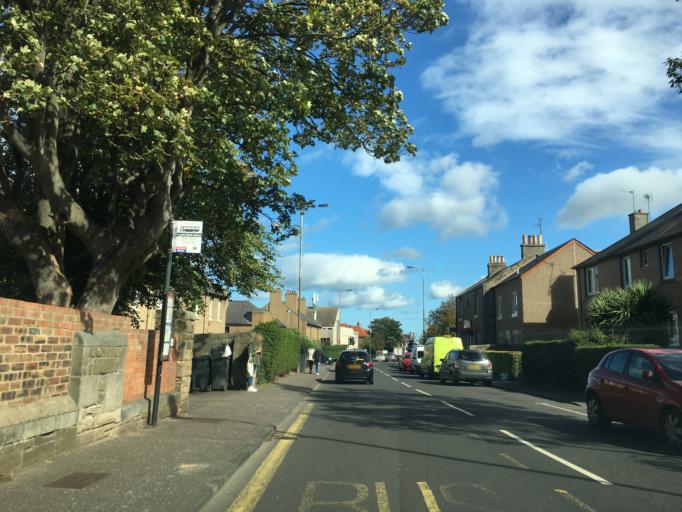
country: GB
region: Scotland
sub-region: Midlothian
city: Loanhead
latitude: 55.9045
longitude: -3.1362
